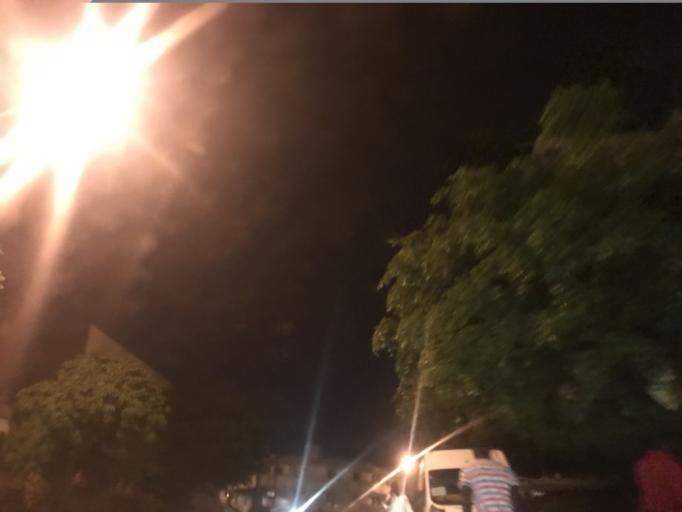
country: SN
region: Dakar
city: Grand Dakar
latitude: 14.7525
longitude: -17.4465
